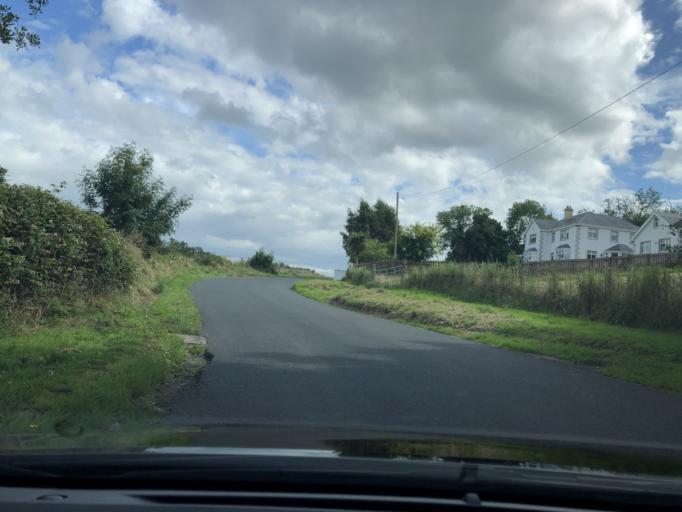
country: GB
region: Northern Ireland
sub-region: Ards District
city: Newtownards
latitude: 54.5854
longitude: -5.7132
